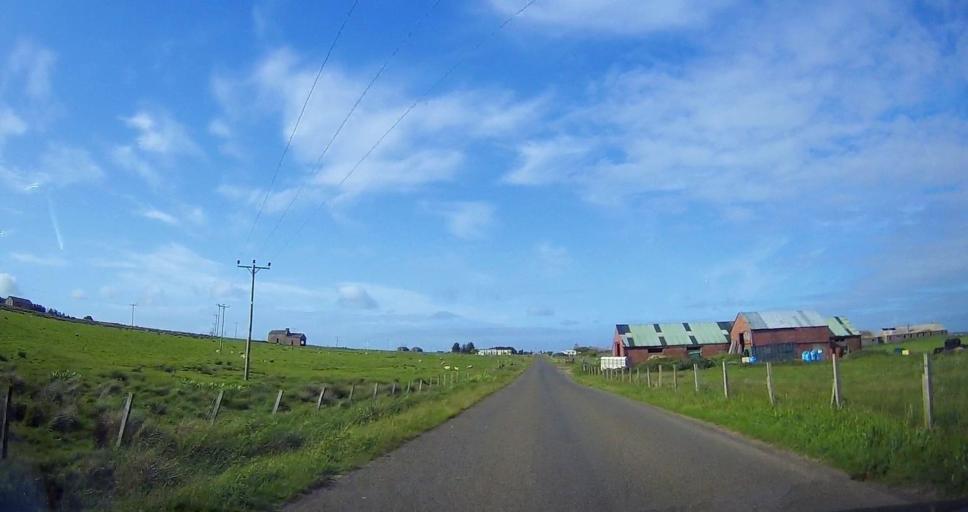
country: GB
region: Scotland
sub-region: Orkney Islands
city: Stromness
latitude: 58.8270
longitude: -3.2087
